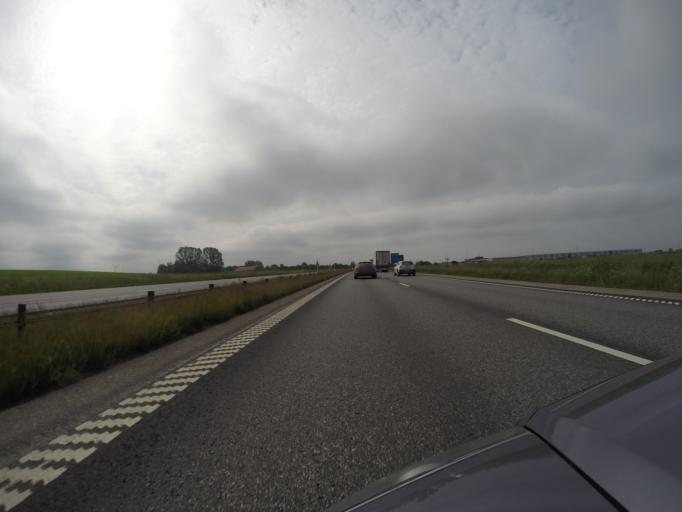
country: SE
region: Skane
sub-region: Landskrona
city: Landskrona
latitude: 55.8860
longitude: 12.8753
